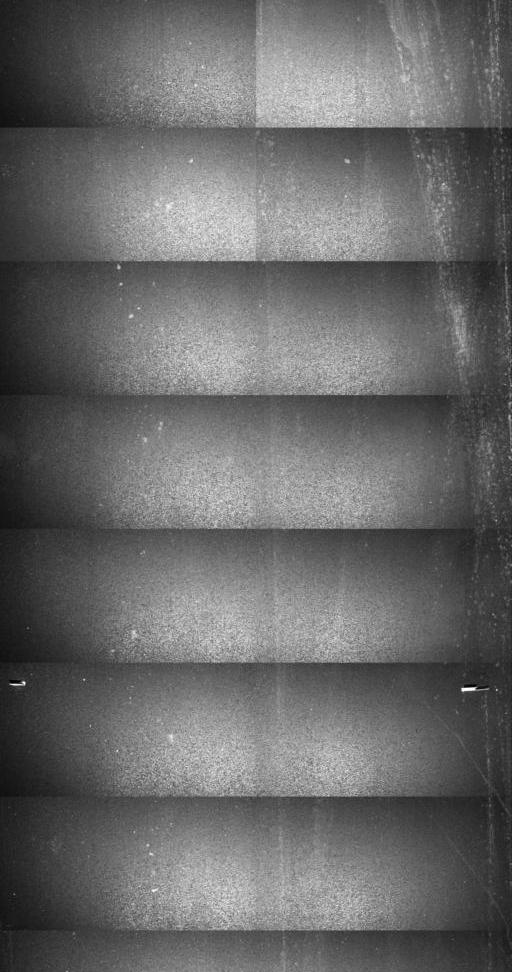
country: US
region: Vermont
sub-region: Franklin County
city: Richford
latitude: 44.9784
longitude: -72.5291
